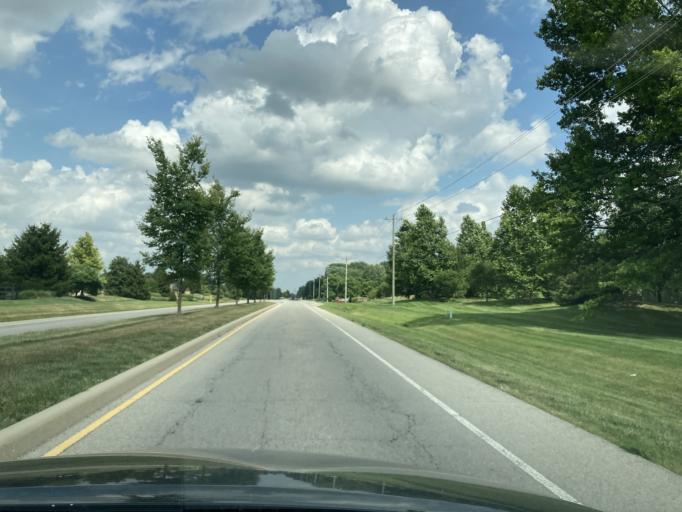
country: US
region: Indiana
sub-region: Boone County
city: Zionsville
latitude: 39.9985
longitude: -86.2582
